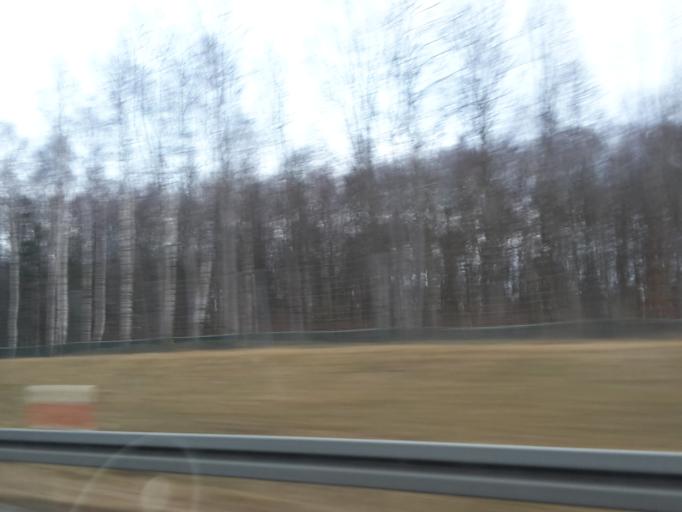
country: PL
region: Warmian-Masurian Voivodeship
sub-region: Powiat ostrodzki
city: Maldyty
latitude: 53.9190
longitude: 19.7205
